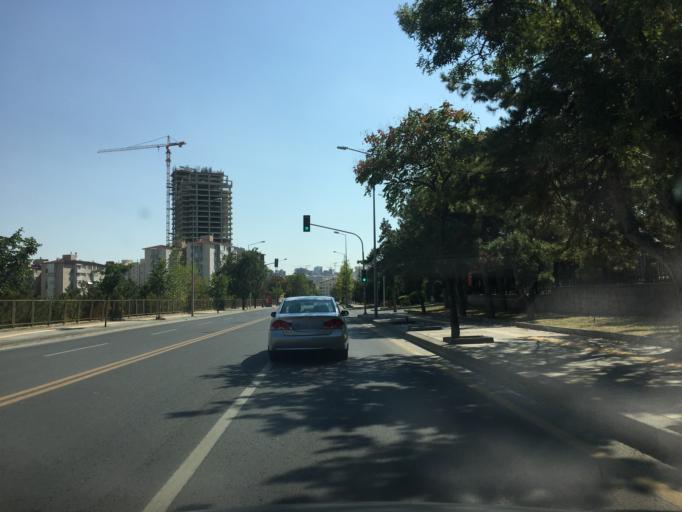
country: TR
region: Ankara
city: Cankaya
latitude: 39.8821
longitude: 32.8665
